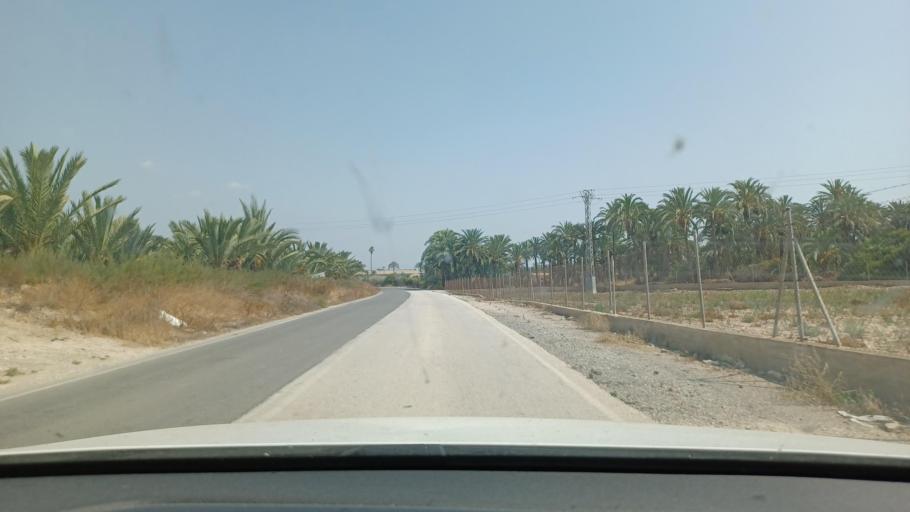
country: ES
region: Valencia
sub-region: Provincia de Alicante
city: Elche
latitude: 38.2458
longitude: -0.6910
